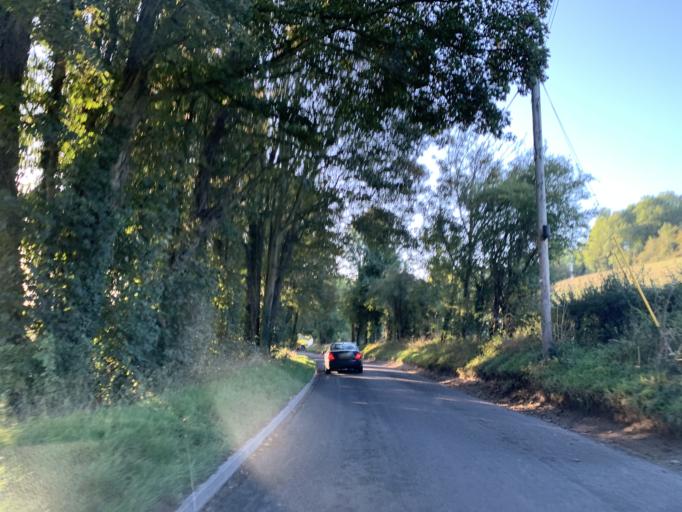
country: GB
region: England
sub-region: Wiltshire
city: Woodford
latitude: 51.1040
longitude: -1.8285
